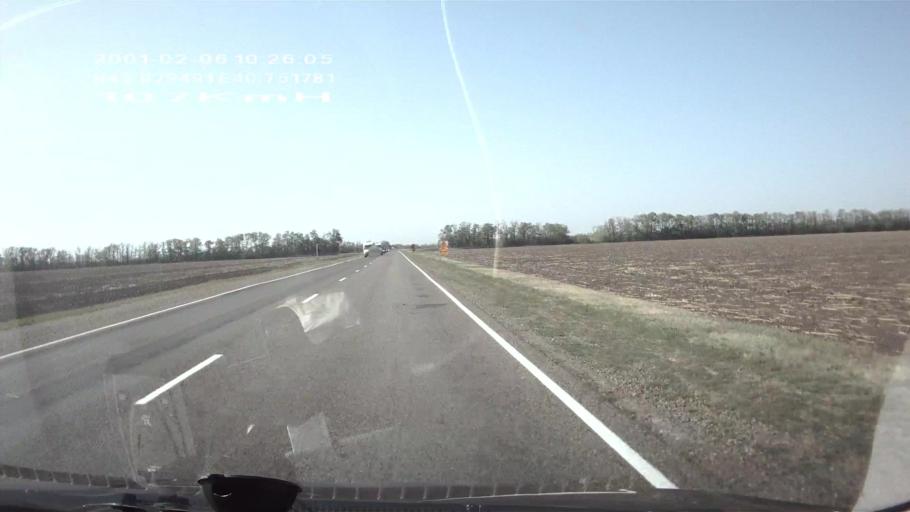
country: RU
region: Krasnodarskiy
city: Novopokrovskaya
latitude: 45.9789
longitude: 40.7509
